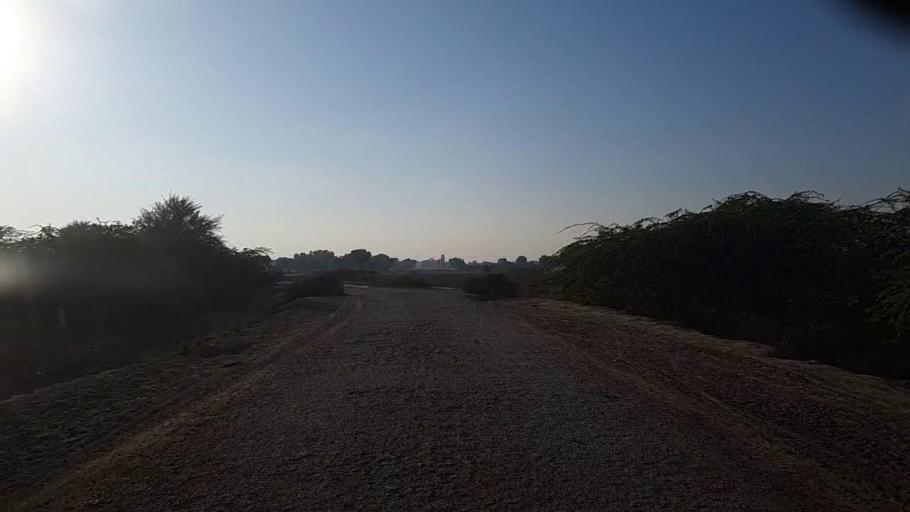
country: PK
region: Sindh
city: Pad Idan
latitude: 26.7345
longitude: 68.3425
